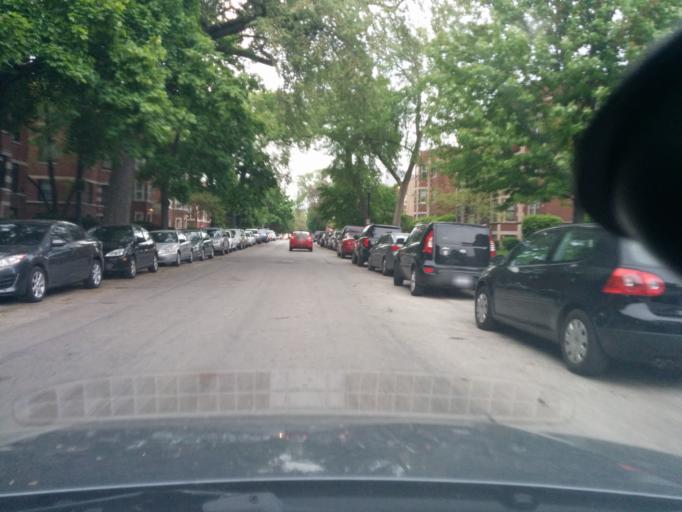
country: US
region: Illinois
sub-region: Cook County
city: Evanston
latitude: 42.0309
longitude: -87.6772
